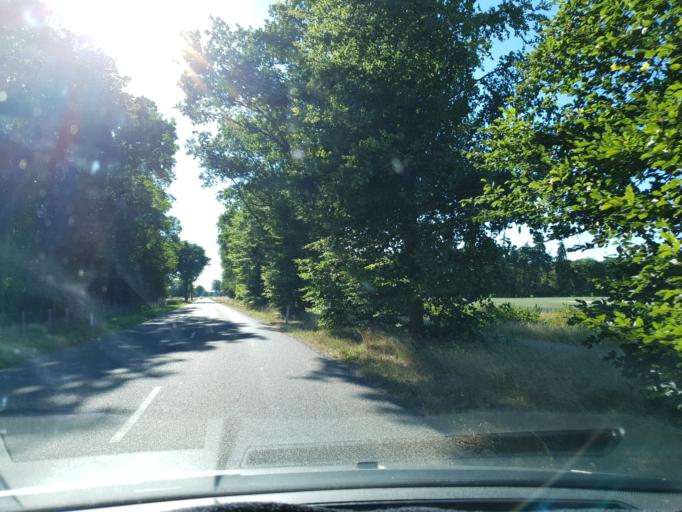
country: NL
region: North Brabant
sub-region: Gemeente Rucphen
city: Rucphen
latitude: 51.4951
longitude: 4.6023
